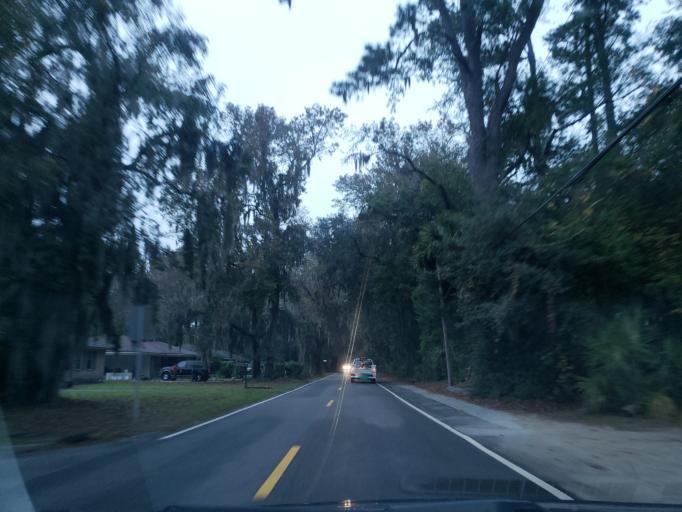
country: US
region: Georgia
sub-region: Chatham County
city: Thunderbolt
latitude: 32.0201
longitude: -81.0678
